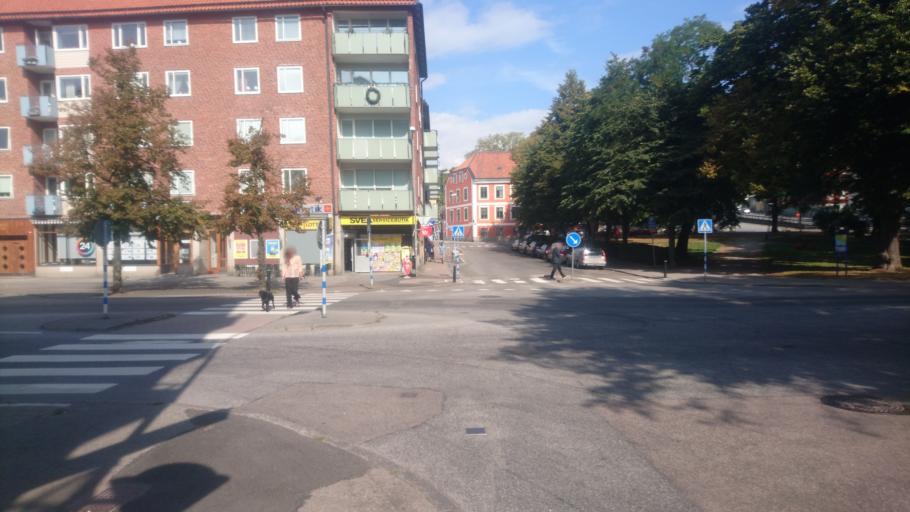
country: SE
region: Blekinge
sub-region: Karlskrona Kommun
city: Karlskrona
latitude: 56.1590
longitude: 15.5856
